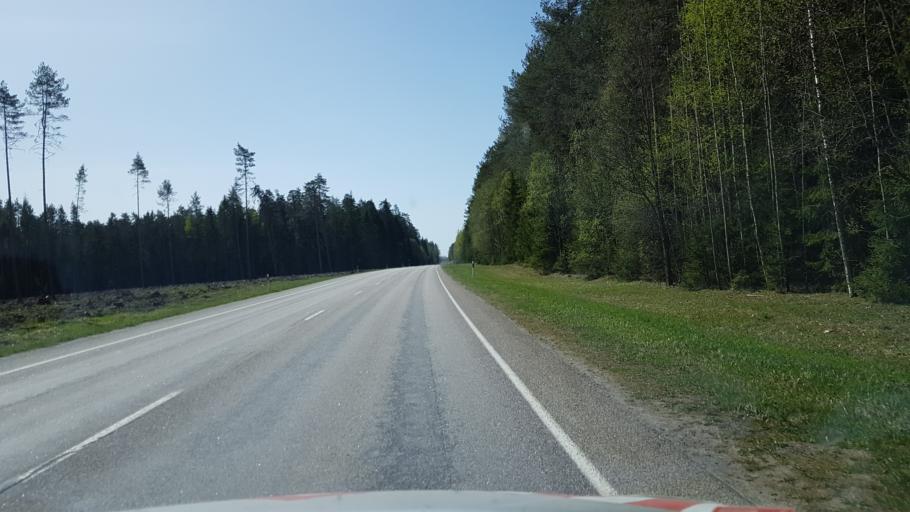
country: EE
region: Valgamaa
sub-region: Valga linn
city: Valga
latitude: 57.8551
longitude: 26.0595
